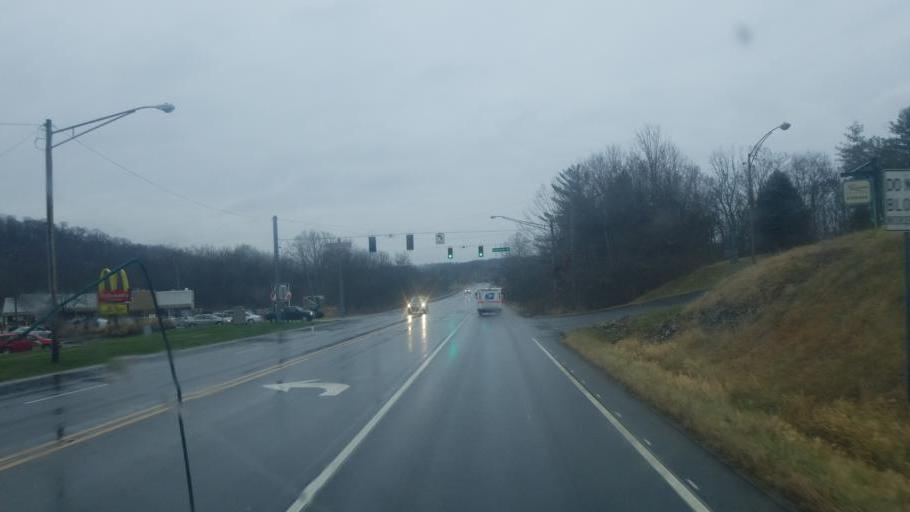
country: US
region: Indiana
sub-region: Brown County
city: Nashville
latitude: 39.2021
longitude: -86.2380
